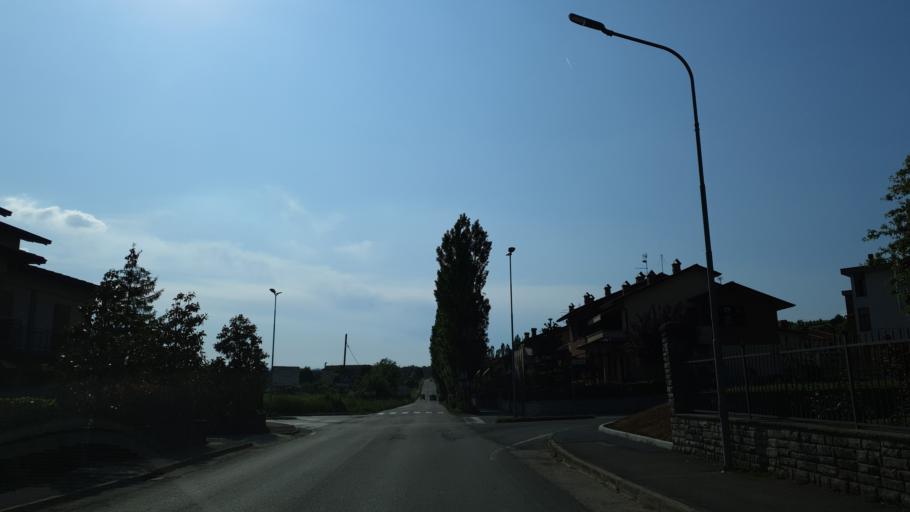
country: IT
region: Tuscany
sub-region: Province of Arezzo
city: Soci
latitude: 43.7370
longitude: 11.8094
